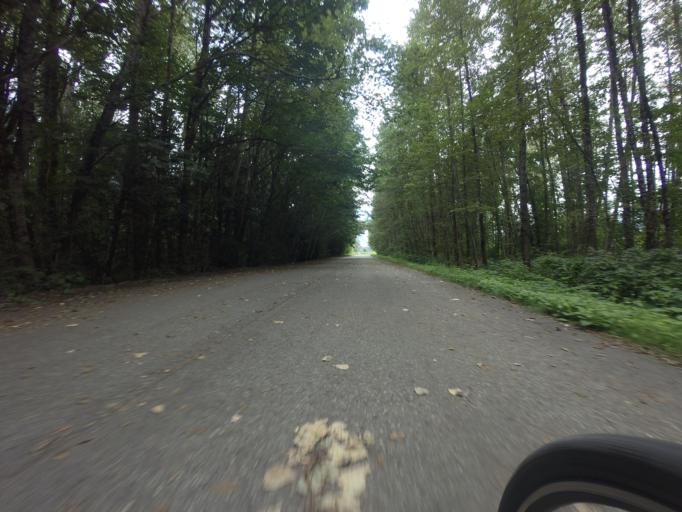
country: CA
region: British Columbia
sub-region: Greater Vancouver Regional District
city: Lions Bay
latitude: 49.7271
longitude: -123.1481
